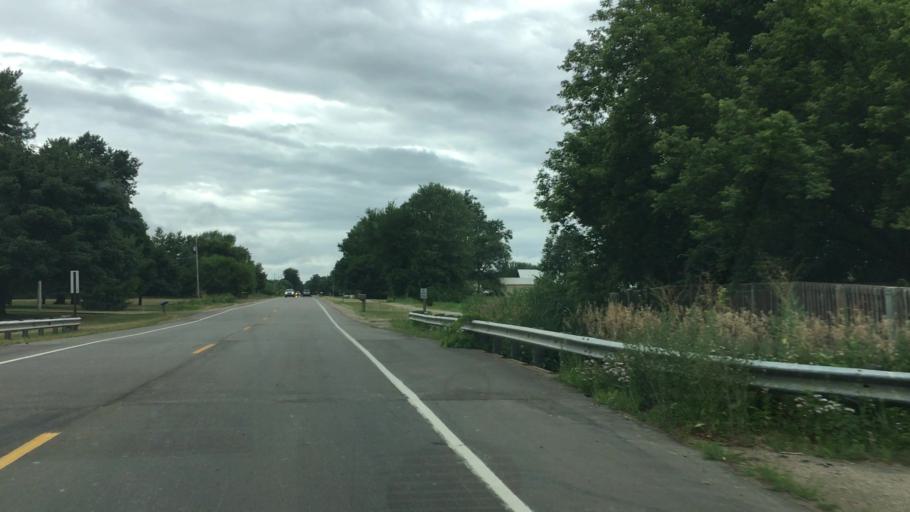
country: US
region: Michigan
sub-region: Ottawa County
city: Zeeland
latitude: 42.7834
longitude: -85.9815
